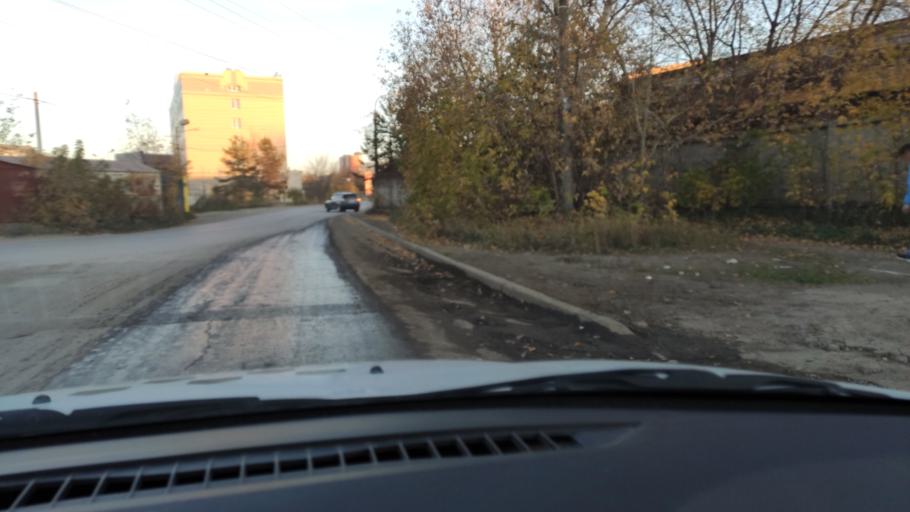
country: RU
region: Perm
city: Kondratovo
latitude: 58.0046
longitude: 56.1517
